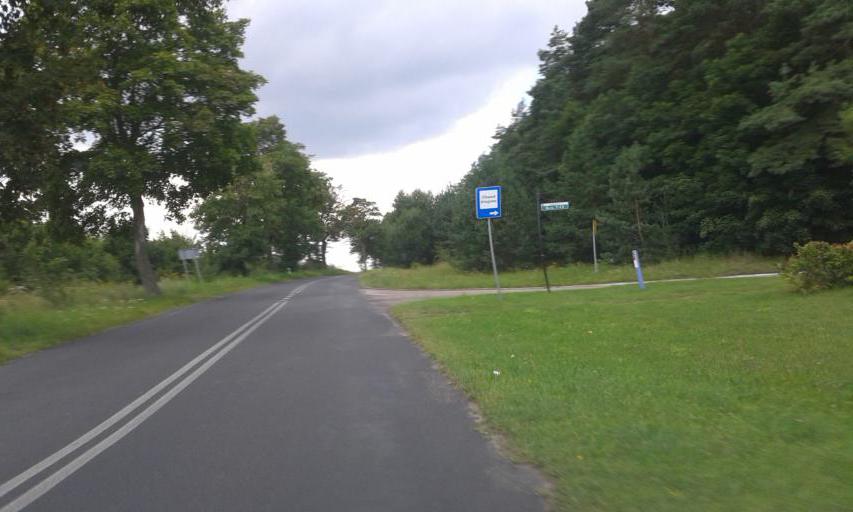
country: PL
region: West Pomeranian Voivodeship
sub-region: Powiat szczecinecki
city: Barwice
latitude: 53.7488
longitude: 16.3238
